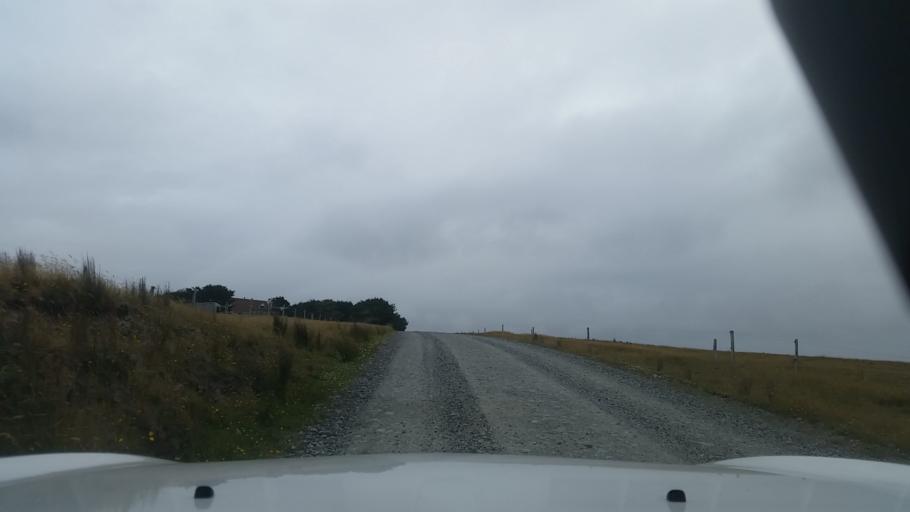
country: NZ
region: Chatham Islands
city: Waitangi
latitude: -43.8048
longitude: -176.6141
